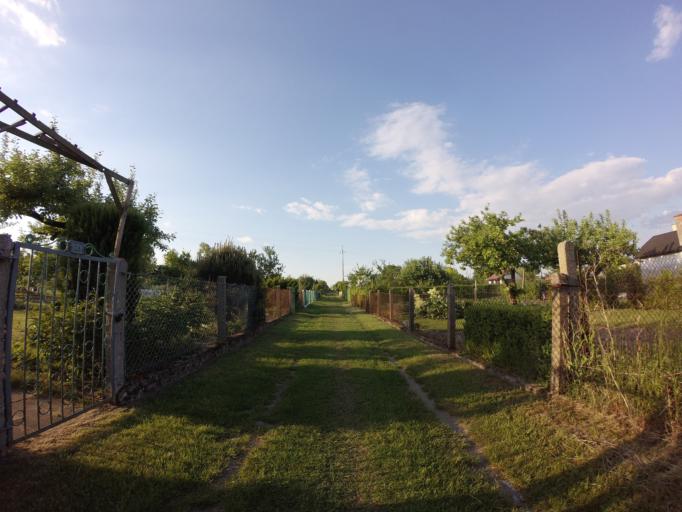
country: PL
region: West Pomeranian Voivodeship
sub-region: Powiat choszczenski
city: Choszczno
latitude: 53.1599
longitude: 15.4000
